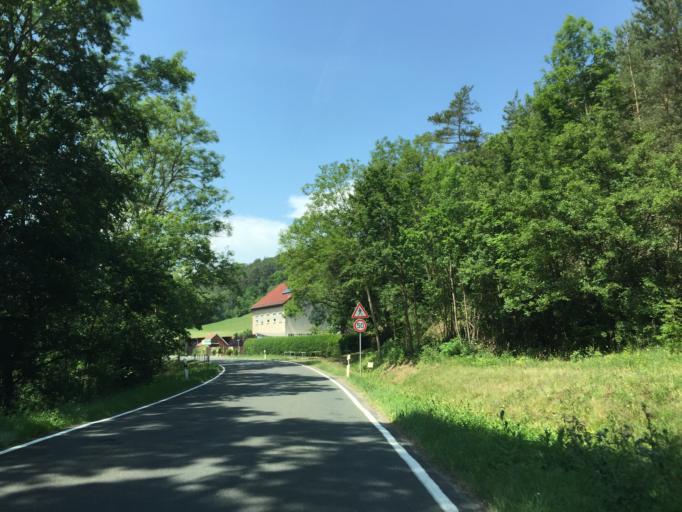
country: DE
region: Thuringia
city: Rittersdorf
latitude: 50.7590
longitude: 11.2614
